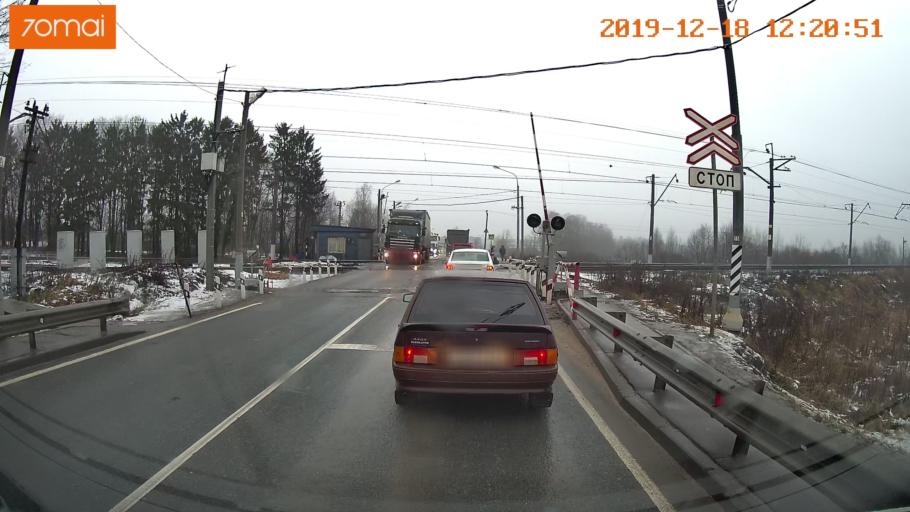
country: RU
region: Moskovskaya
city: Novopetrovskoye
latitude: 55.9967
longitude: 36.4743
